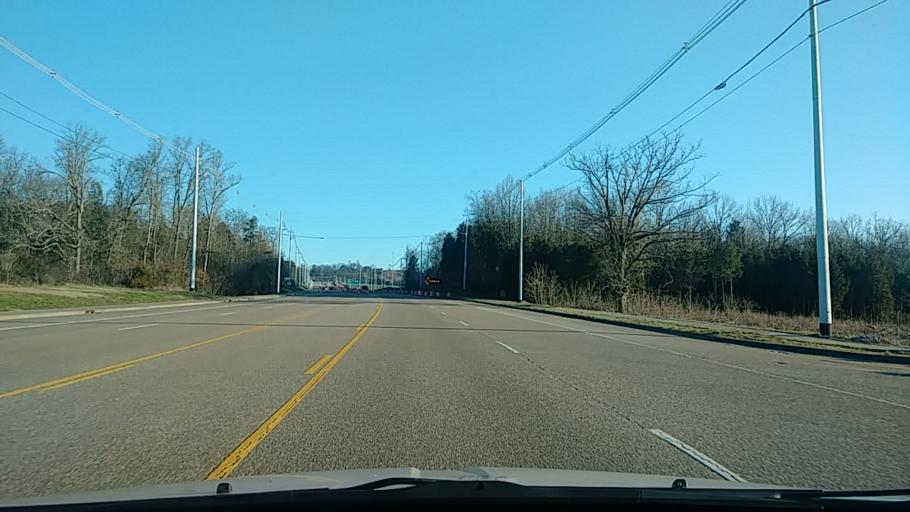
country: US
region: Tennessee
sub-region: Hamblen County
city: Morristown
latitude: 36.1815
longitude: -83.3527
